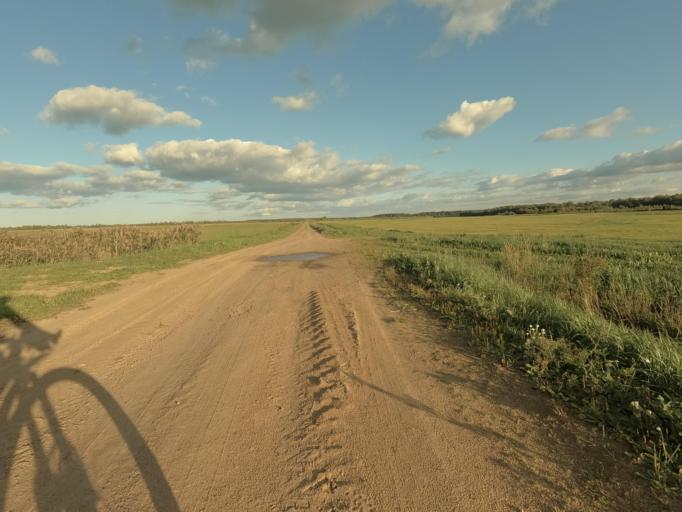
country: RU
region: Leningrad
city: Imeni Sverdlova
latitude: 59.8620
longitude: 30.7476
